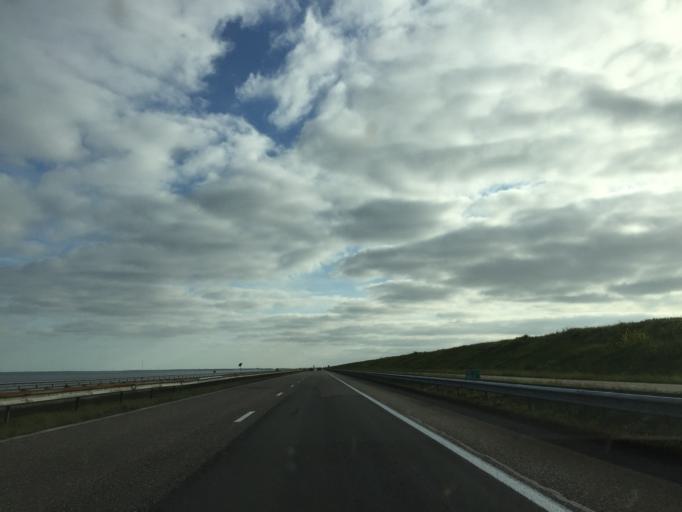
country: NL
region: North Holland
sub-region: Gemeente Hollands Kroon
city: Den Oever
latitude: 52.9857
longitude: 5.1400
